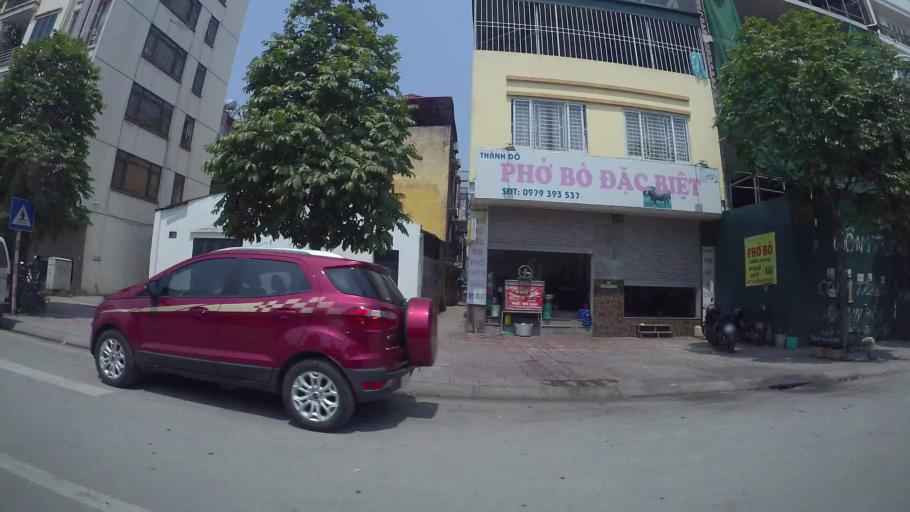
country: VN
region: Ha Noi
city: Hoan Kiem
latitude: 21.0419
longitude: 105.8739
